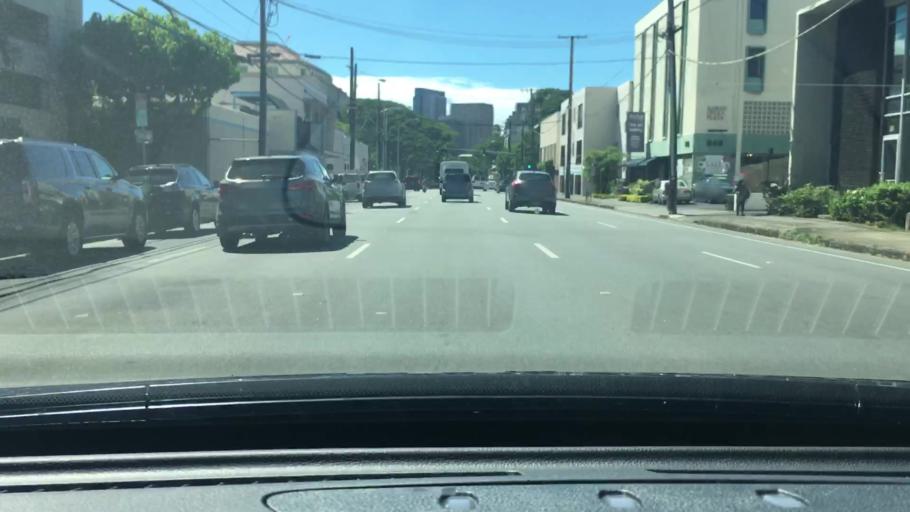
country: US
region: Hawaii
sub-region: Honolulu County
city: Honolulu
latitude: 21.3040
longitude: -157.8498
